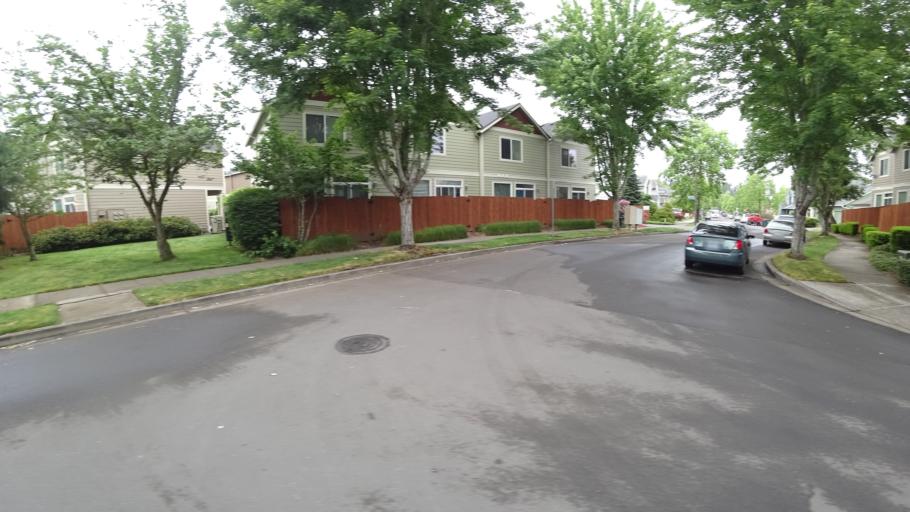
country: US
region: Oregon
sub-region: Washington County
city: Rockcreek
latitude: 45.5286
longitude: -122.8898
